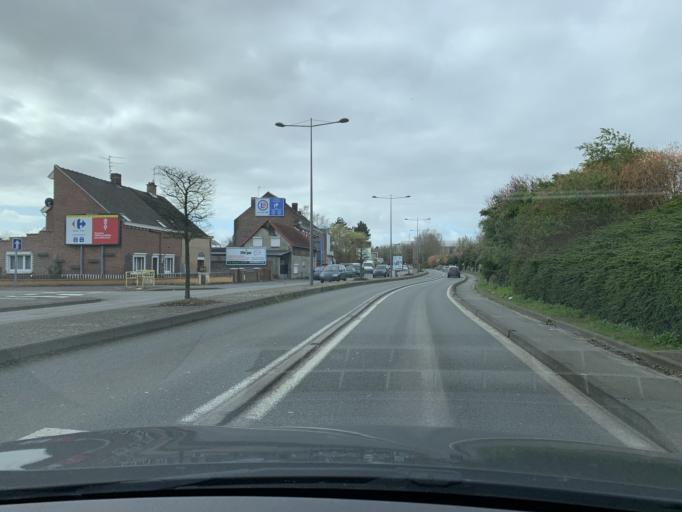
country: FR
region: Nord-Pas-de-Calais
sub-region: Departement du Nord
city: Waziers
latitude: 50.3864
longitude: 3.0997
